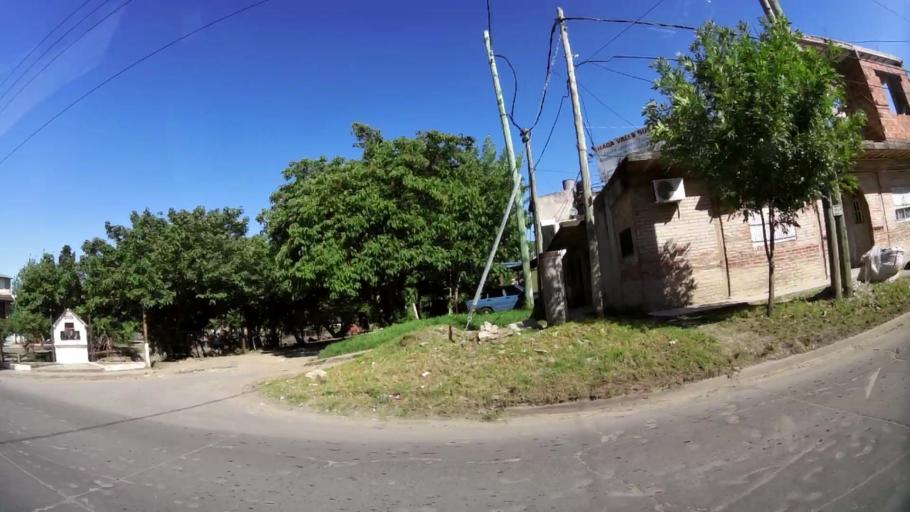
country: AR
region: Buenos Aires
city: Caseros
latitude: -34.5448
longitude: -58.5927
